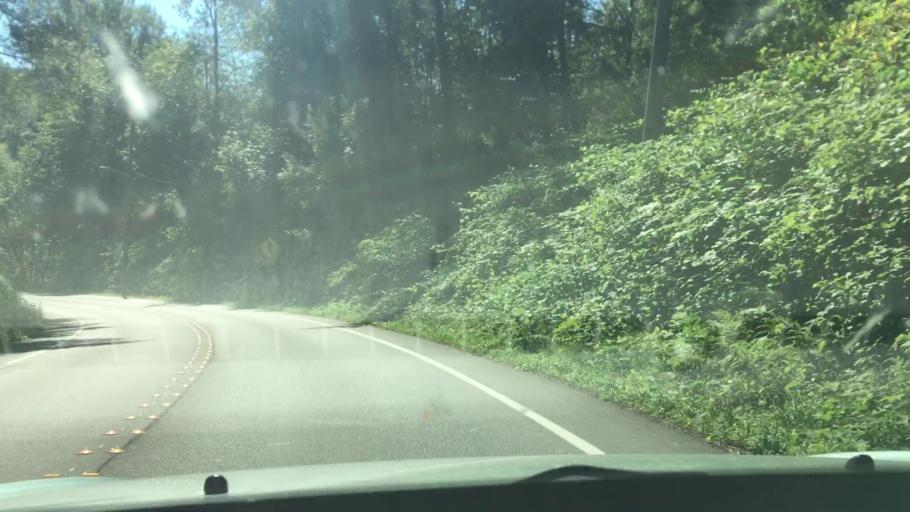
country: US
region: Washington
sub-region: King County
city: Newcastle
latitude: 47.5352
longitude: -122.1313
